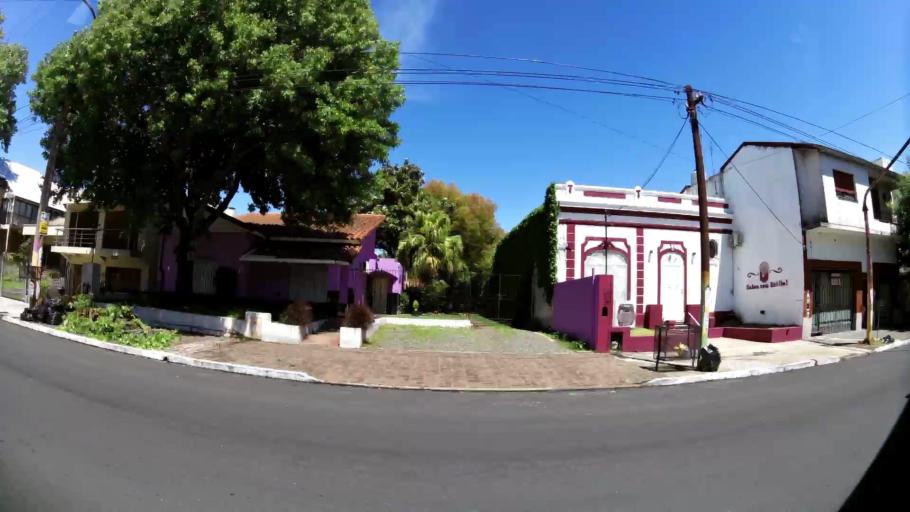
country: AR
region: Buenos Aires
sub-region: Partido de Quilmes
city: Quilmes
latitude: -34.7224
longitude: -58.2662
